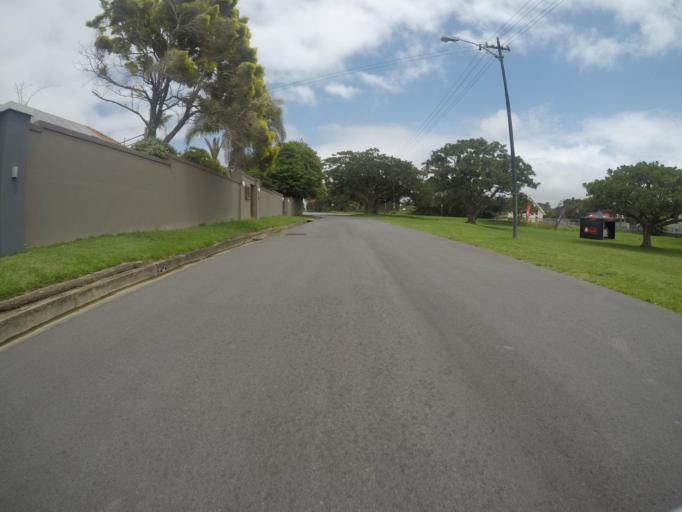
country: ZA
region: Eastern Cape
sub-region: Buffalo City Metropolitan Municipality
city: East London
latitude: -32.9893
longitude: 27.9271
